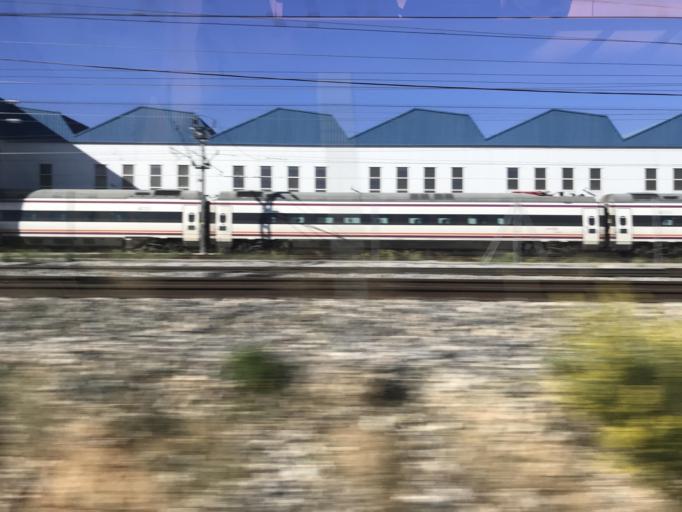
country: ES
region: Madrid
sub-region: Provincia de Madrid
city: Las Tablas
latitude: 40.4952
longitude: -3.6781
